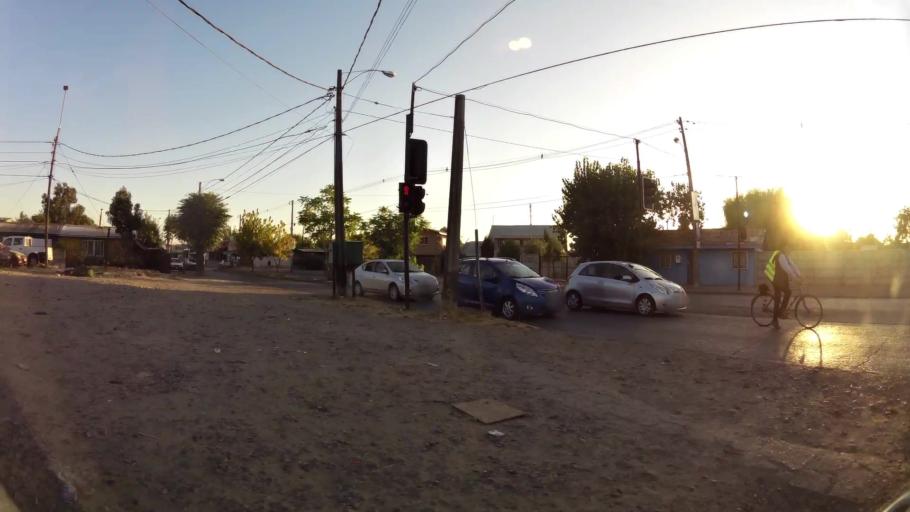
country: CL
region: Maule
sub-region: Provincia de Talca
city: Talca
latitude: -35.4493
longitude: -71.6605
